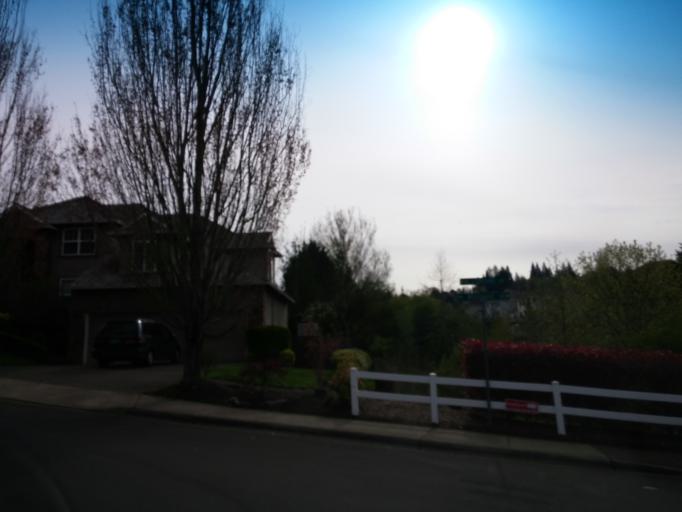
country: US
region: Oregon
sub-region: Washington County
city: Cedar Mill
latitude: 45.5385
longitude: -122.8101
